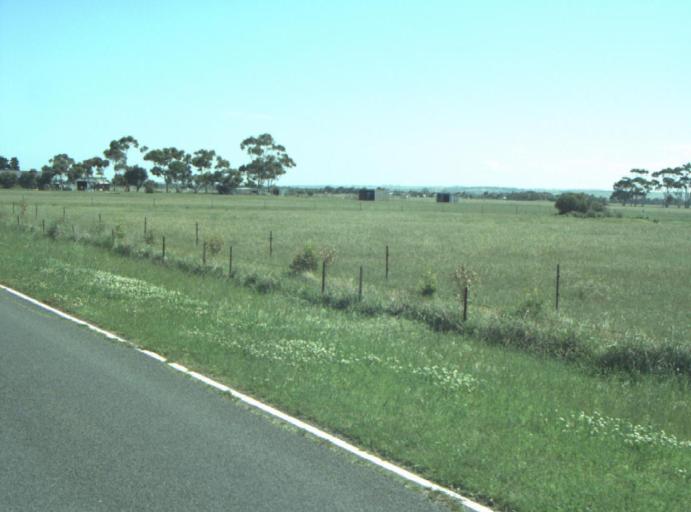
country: AU
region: Victoria
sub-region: Greater Geelong
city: Lara
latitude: -37.9905
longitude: 144.4022
